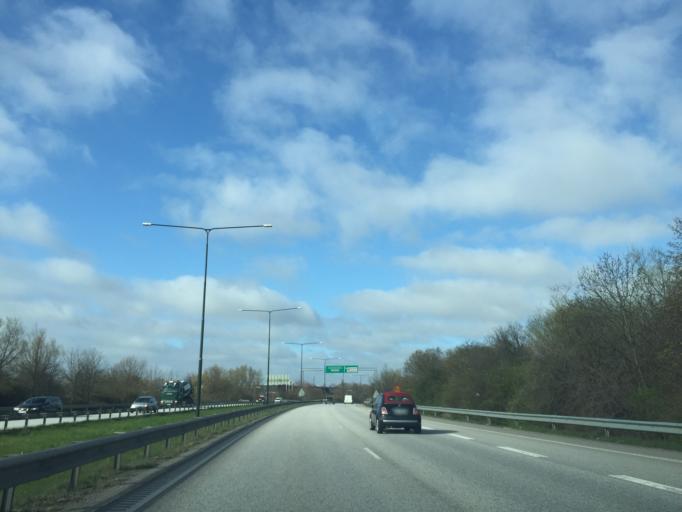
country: SE
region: Skane
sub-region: Malmo
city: Malmoe
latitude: 55.5665
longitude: 13.0390
